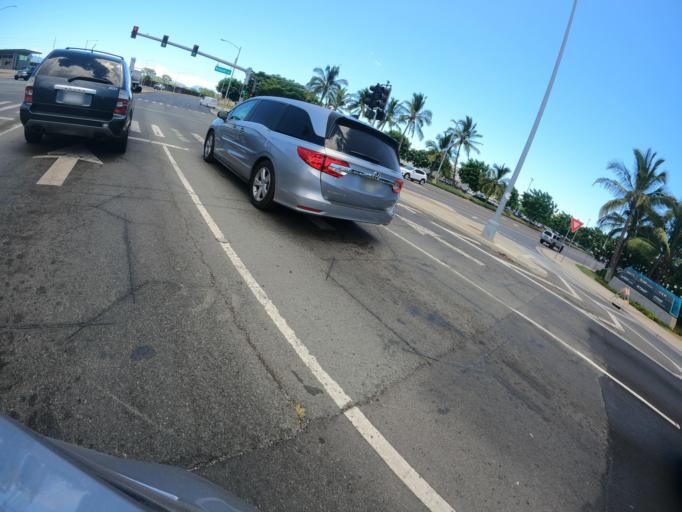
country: US
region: Hawaii
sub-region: Honolulu County
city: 'Ewa Villages
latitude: 21.3356
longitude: -158.0546
